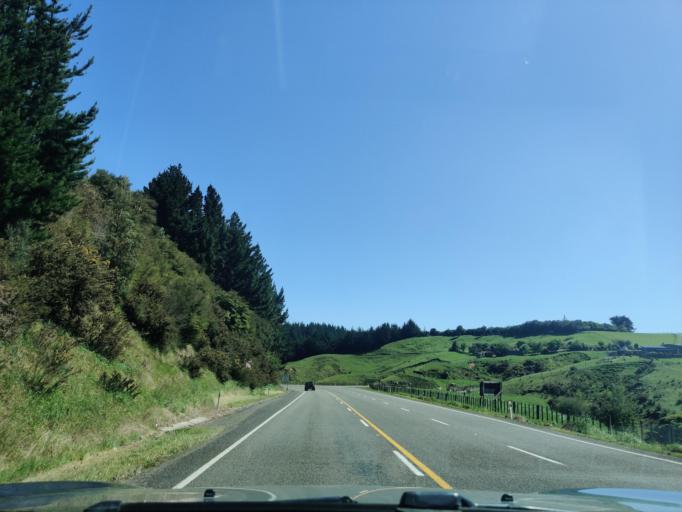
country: NZ
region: Manawatu-Wanganui
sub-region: Wanganui District
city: Wanganui
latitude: -39.8351
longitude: 174.9095
